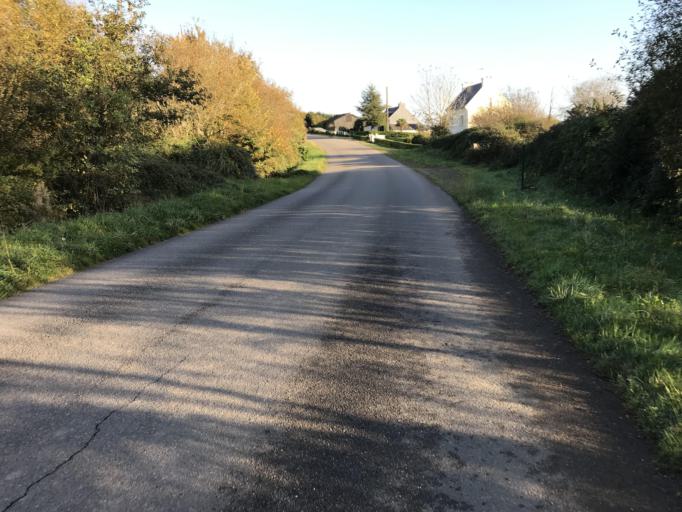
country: FR
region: Brittany
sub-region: Departement du Finistere
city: Le Faou
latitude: 48.2995
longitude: -4.2105
